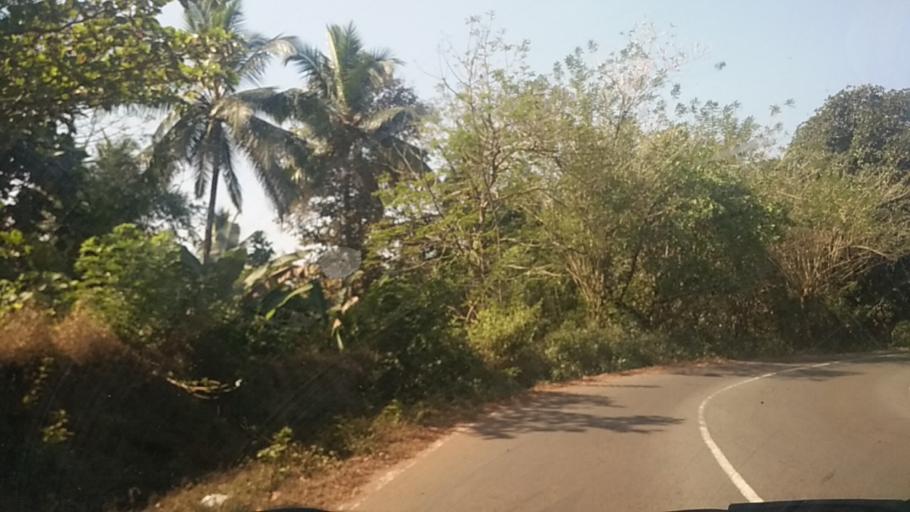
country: IN
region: Goa
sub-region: South Goa
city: Sanguem
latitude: 15.2215
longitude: 74.1639
